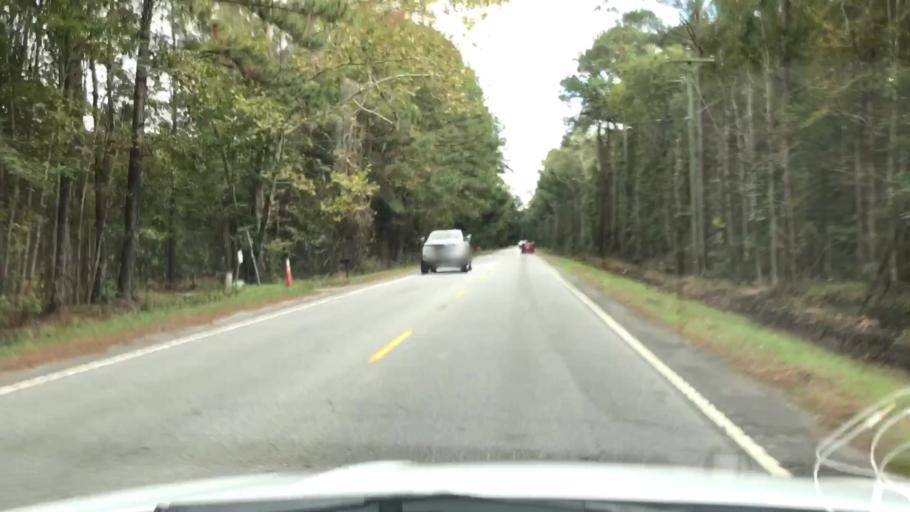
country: US
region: South Carolina
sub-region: Beaufort County
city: Bluffton
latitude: 32.2307
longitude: -80.9178
